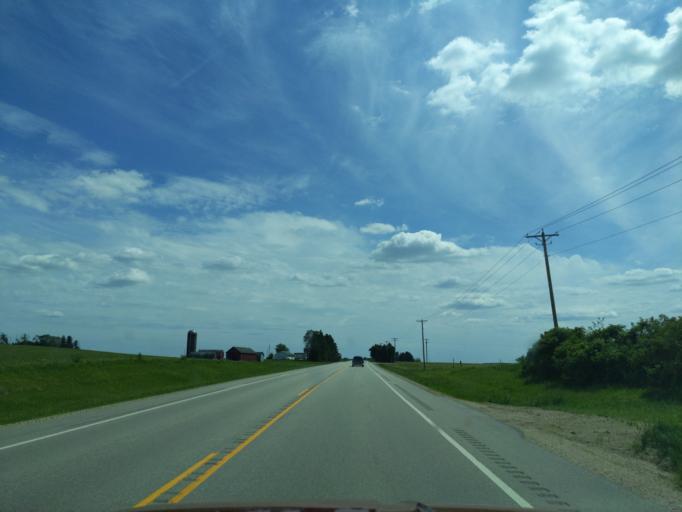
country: US
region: Wisconsin
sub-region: Columbia County
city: Poynette
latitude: 43.3665
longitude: -89.3283
